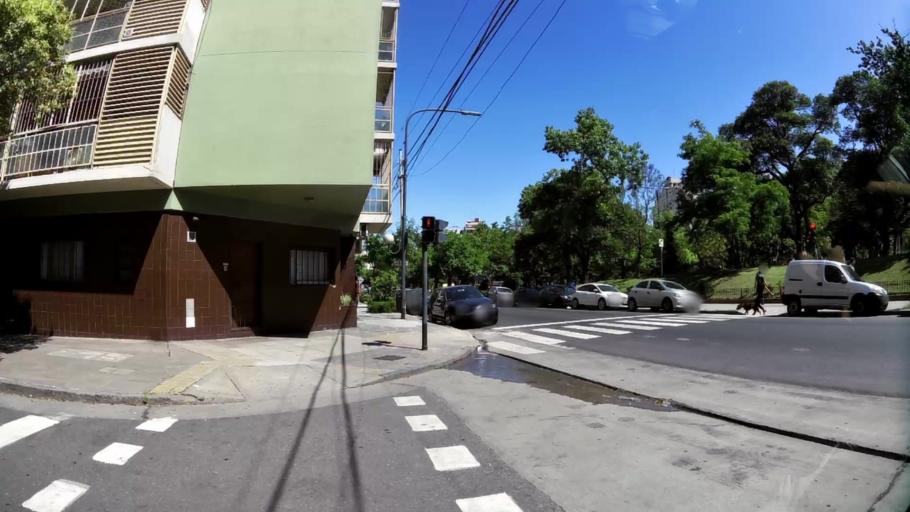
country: AR
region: Buenos Aires F.D.
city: Villa Santa Rita
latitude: -34.6335
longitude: -58.4401
